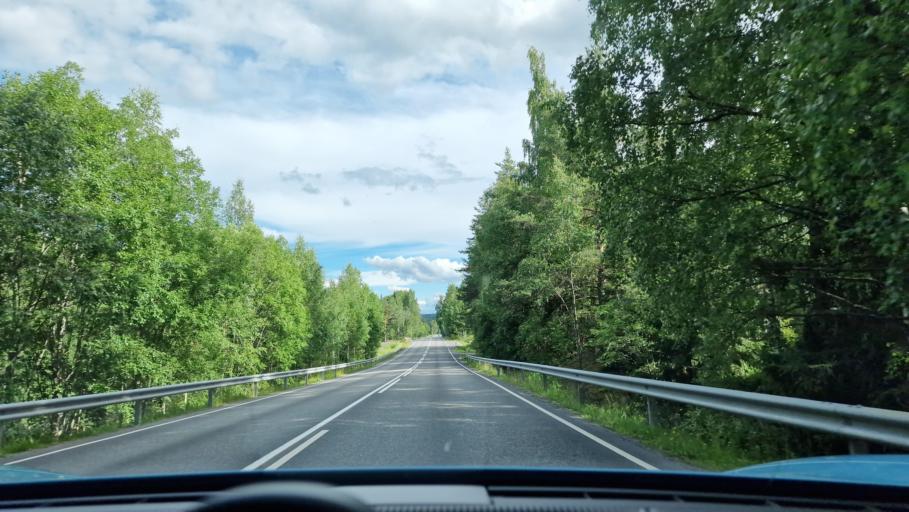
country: FI
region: Pirkanmaa
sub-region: Tampere
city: Orivesi
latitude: 61.6156
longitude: 24.3018
